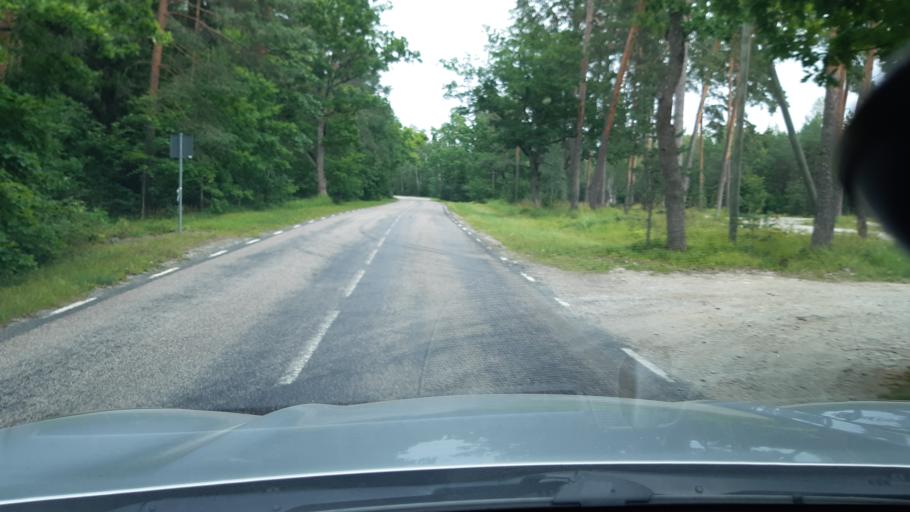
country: EE
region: Raplamaa
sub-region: Maerjamaa vald
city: Marjamaa
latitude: 59.0398
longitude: 24.5047
